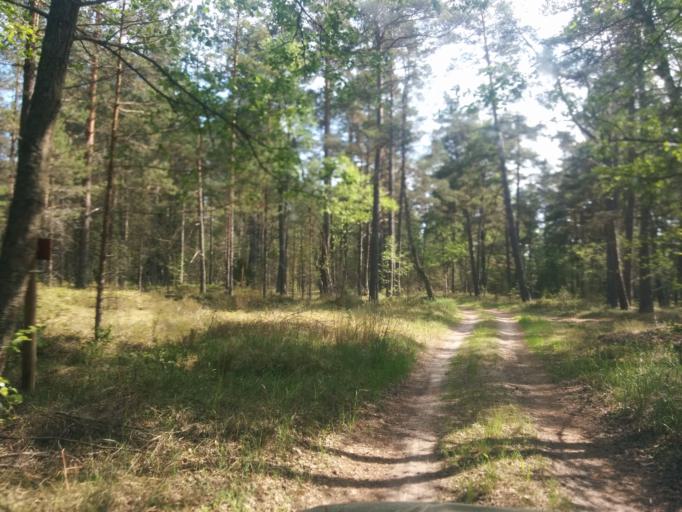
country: LV
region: Dundaga
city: Dundaga
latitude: 57.6196
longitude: 22.0849
